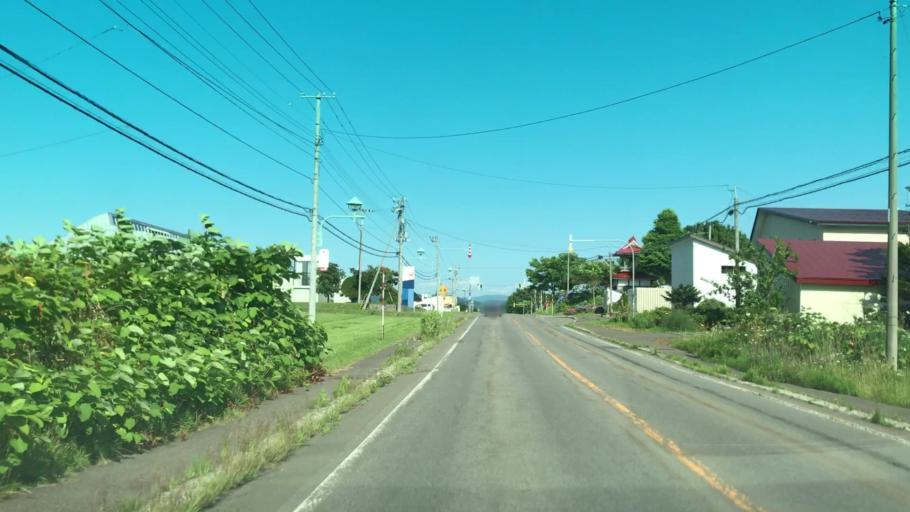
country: JP
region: Hokkaido
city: Iwanai
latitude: 42.9799
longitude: 140.6038
